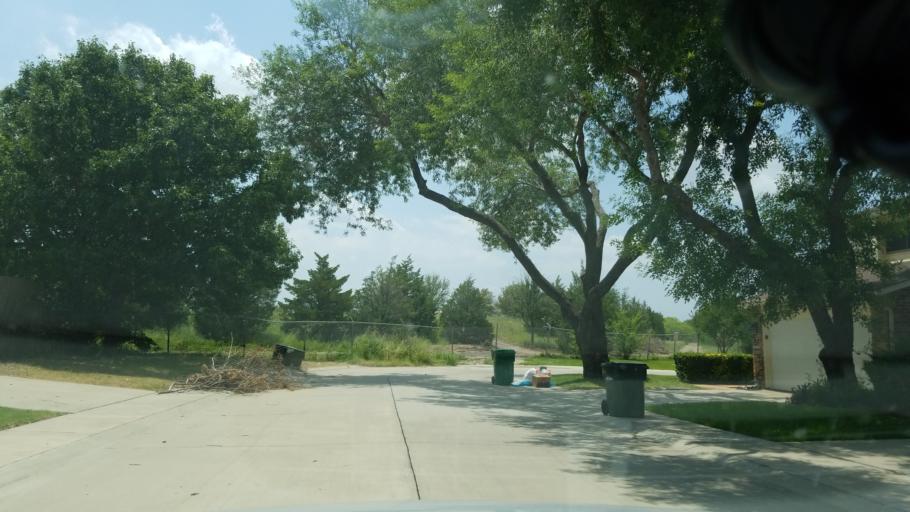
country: US
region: Texas
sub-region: Dallas County
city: Carrollton
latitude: 32.9664
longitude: -96.8656
